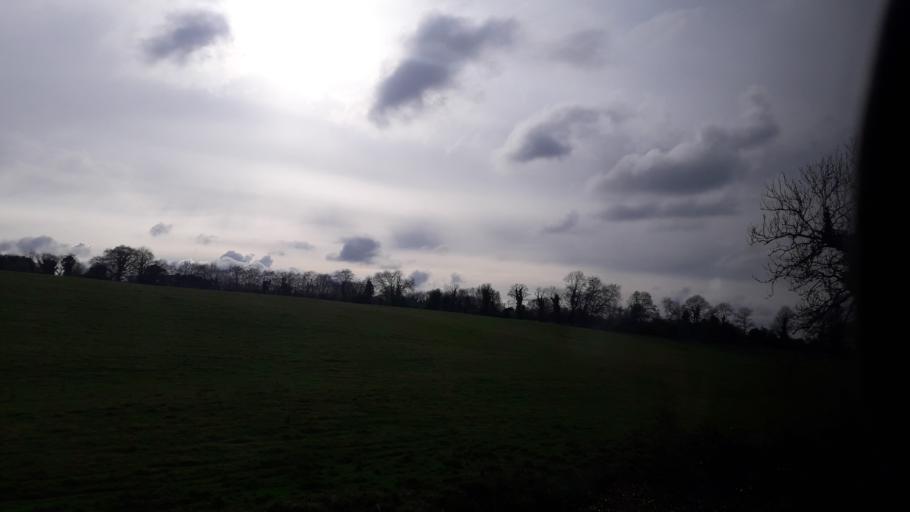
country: IE
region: Leinster
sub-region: Kildare
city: Kilcock
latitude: 53.4148
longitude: -6.6965
